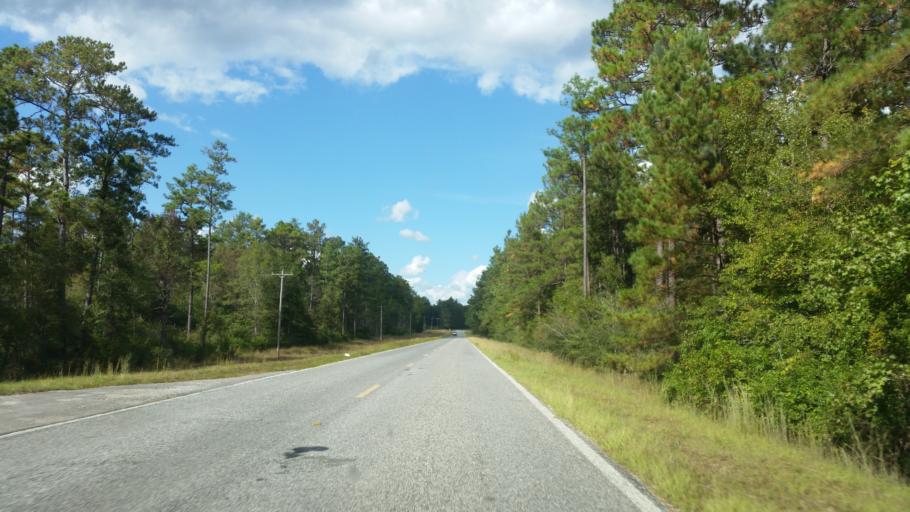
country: US
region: Mississippi
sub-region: Stone County
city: Wiggins
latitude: 30.9721
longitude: -89.0564
